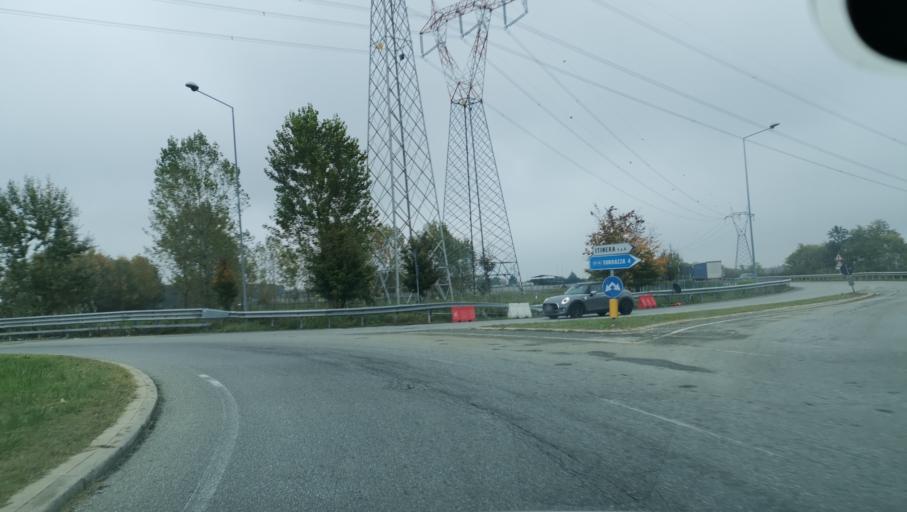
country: IT
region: Piedmont
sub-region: Provincia di Torino
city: Rondissone
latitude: 45.2353
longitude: 7.9565
